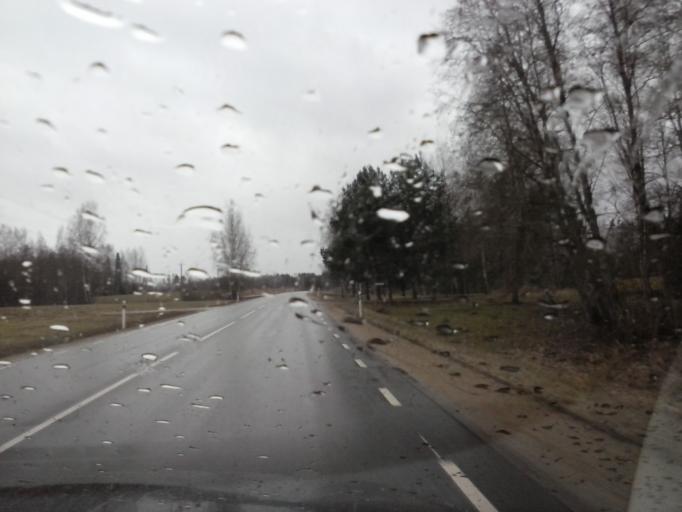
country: EE
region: Polvamaa
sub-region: Polva linn
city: Polva
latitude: 58.0518
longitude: 27.0769
